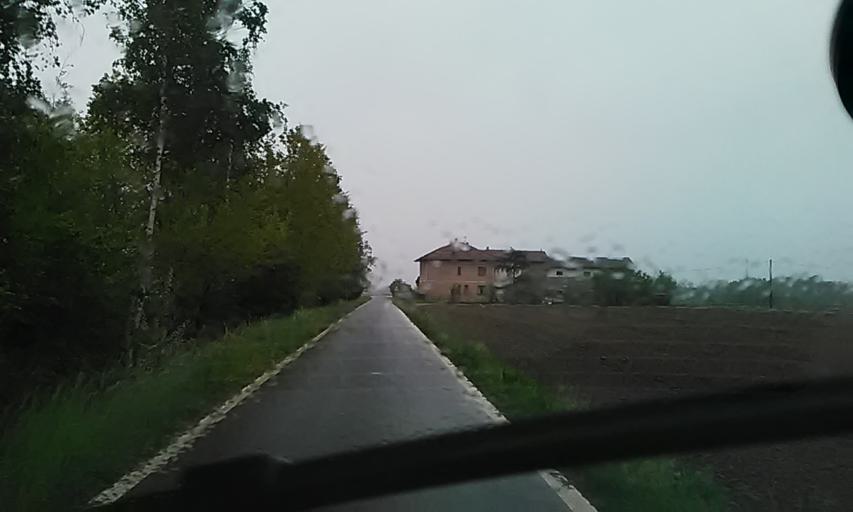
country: IT
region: Piedmont
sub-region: Provincia di Vercelli
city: San Giacomo Vercellese
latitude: 45.4981
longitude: 8.3351
